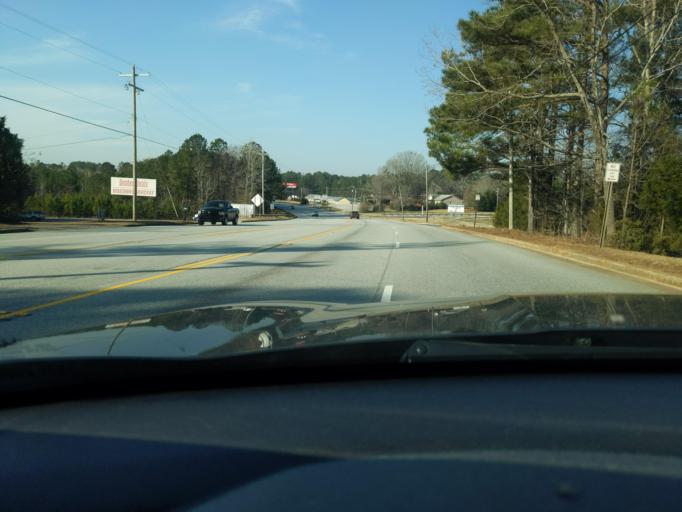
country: US
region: South Carolina
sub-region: Abbeville County
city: Abbeville
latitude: 34.1865
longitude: -82.3502
